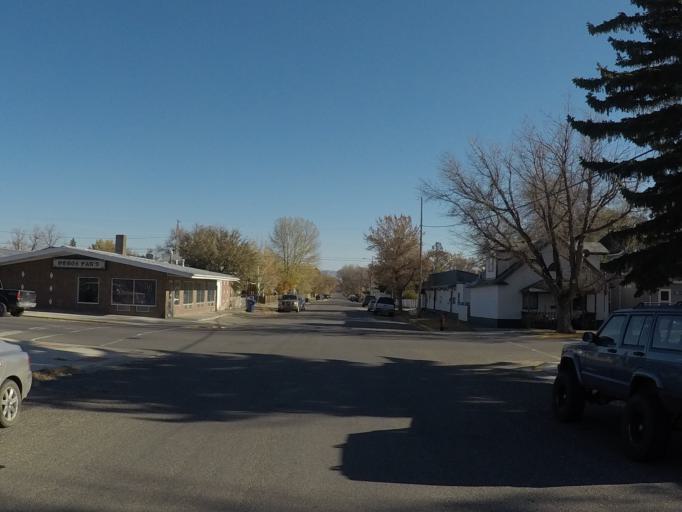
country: US
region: Montana
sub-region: Park County
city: Livingston
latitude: 45.6599
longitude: -110.5569
